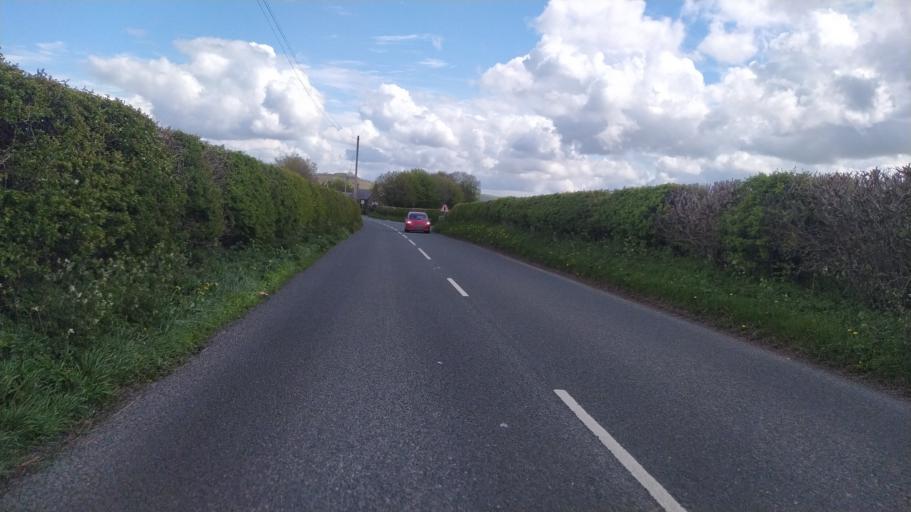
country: GB
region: England
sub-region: Wiltshire
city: Kilmington
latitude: 51.1154
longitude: -2.3077
